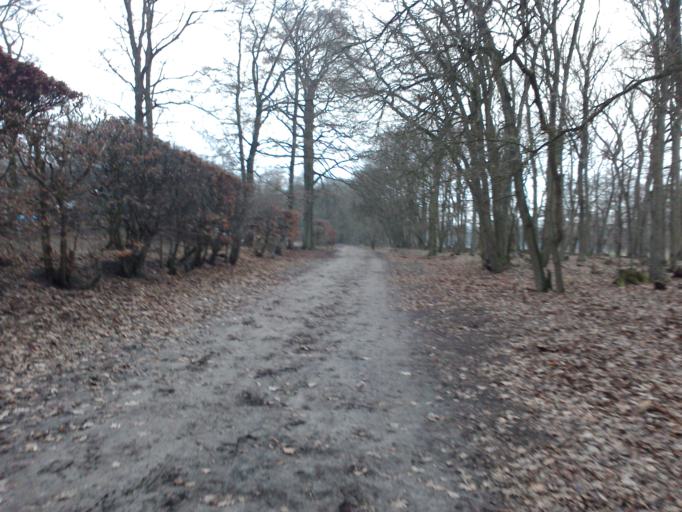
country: NL
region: Utrecht
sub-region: Gemeente De Bilt
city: De Bilt
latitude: 52.1112
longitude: 5.2006
